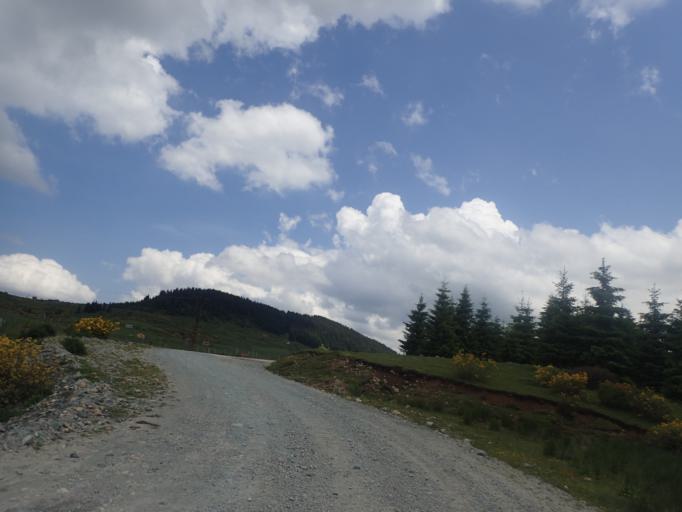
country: TR
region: Ordu
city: Topcam
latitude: 40.6833
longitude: 37.9358
